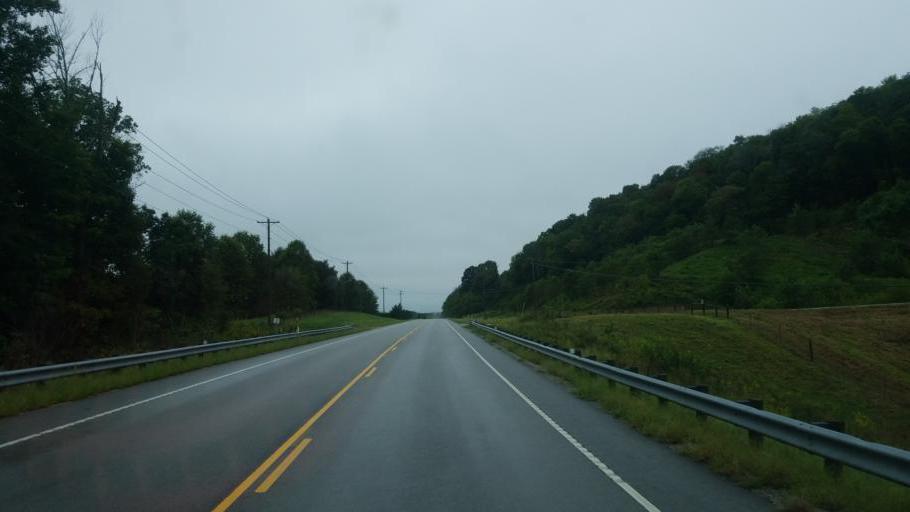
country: US
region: Ohio
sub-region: Adams County
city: Manchester
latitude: 38.6388
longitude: -83.6512
